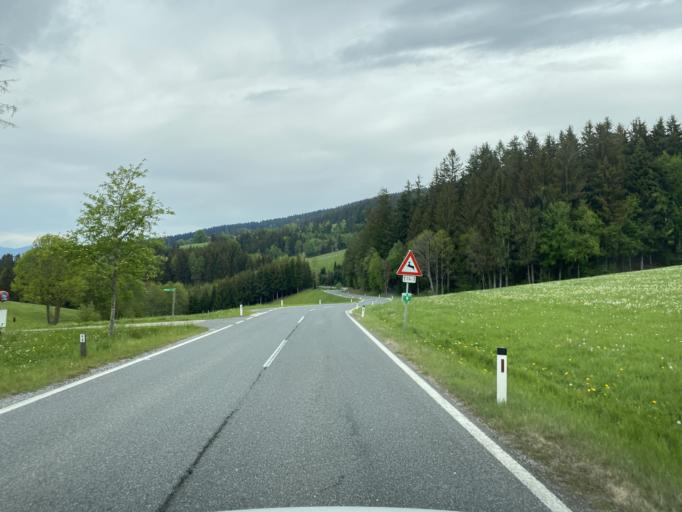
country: AT
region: Styria
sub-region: Politischer Bezirk Weiz
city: Gschaid bei Birkfeld
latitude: 47.3417
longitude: 15.7437
